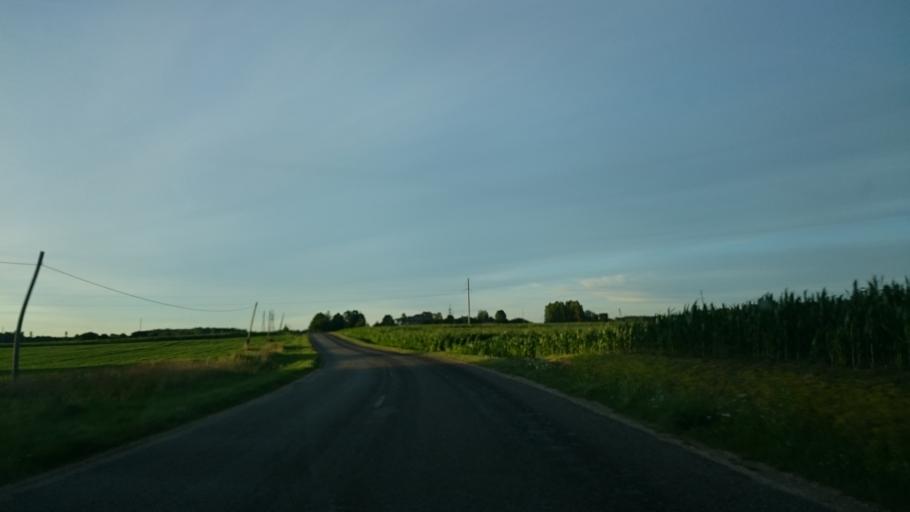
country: LV
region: Saldus Rajons
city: Saldus
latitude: 56.6831
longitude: 22.5024
